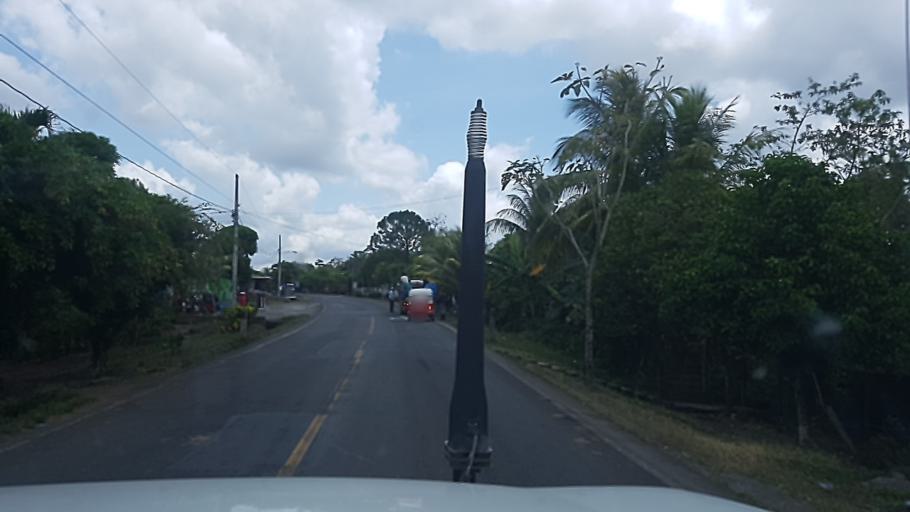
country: NI
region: Atlantico Sur
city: Muelle de los Bueyes
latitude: 11.9148
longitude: -84.6446
